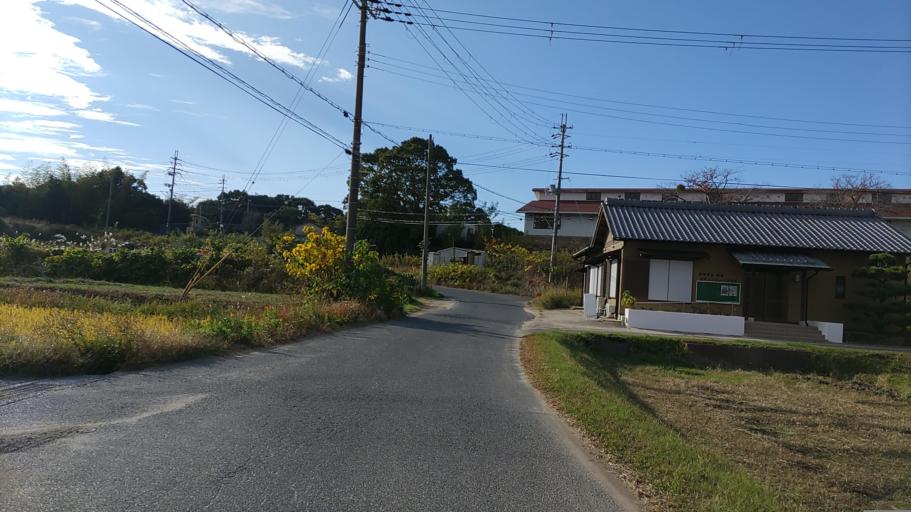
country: JP
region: Hyogo
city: Sumoto
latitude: 34.3892
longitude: 134.8106
